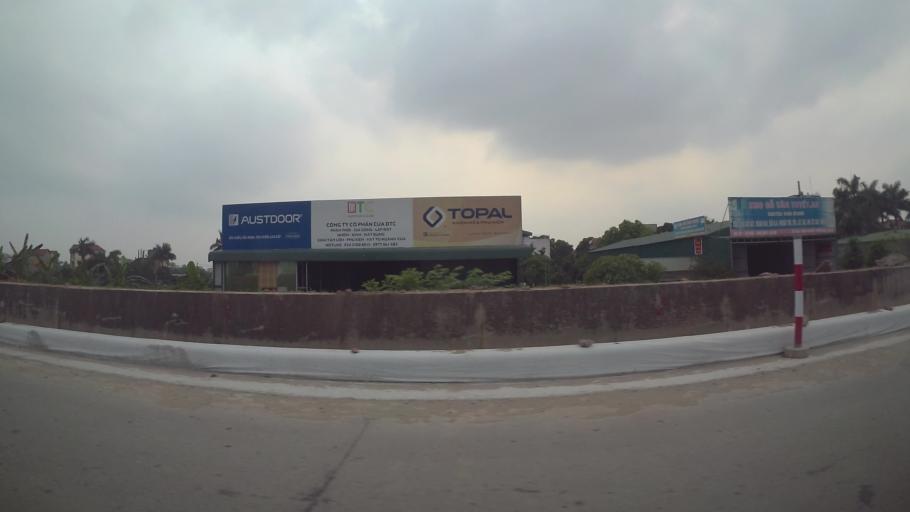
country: VN
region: Ha Noi
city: Trau Quy
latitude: 21.0100
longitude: 105.9050
